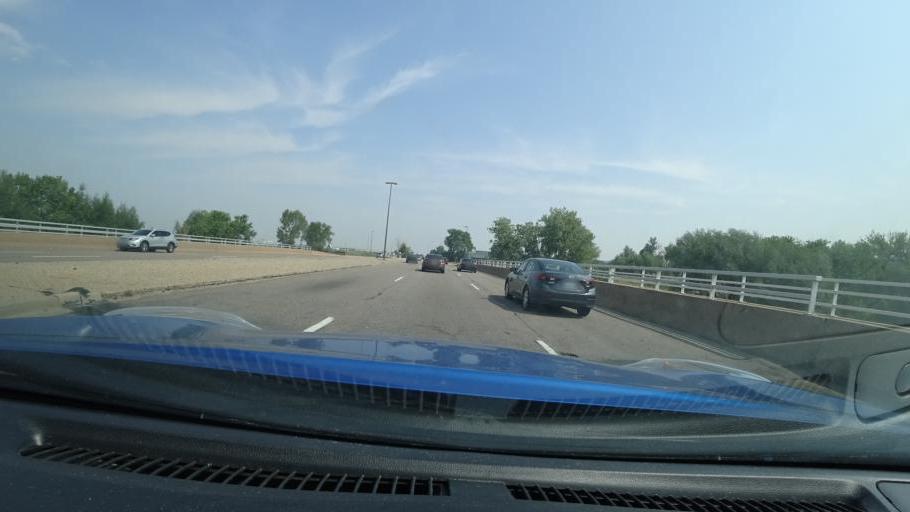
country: US
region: Colorado
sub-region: Adams County
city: Aurora
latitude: 39.7474
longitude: -104.7912
